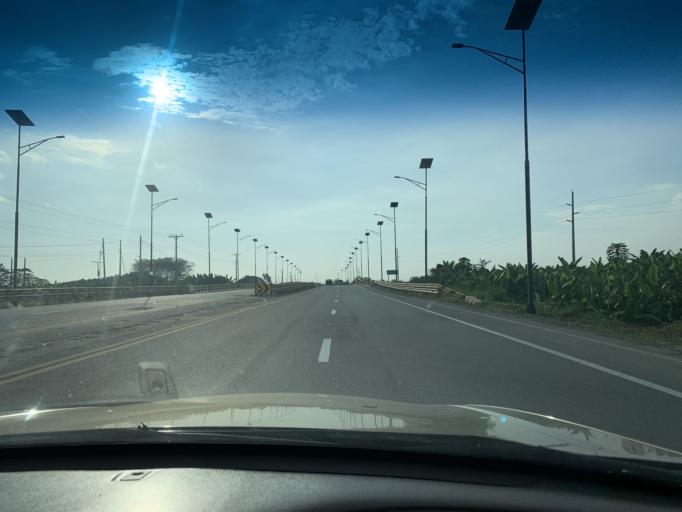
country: EC
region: Guayas
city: Naranjito
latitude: -2.2581
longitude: -79.5564
